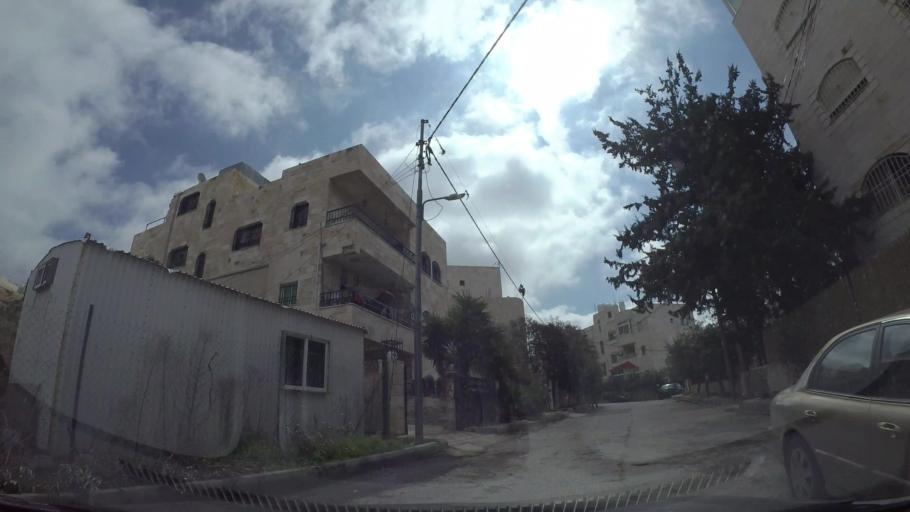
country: JO
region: Amman
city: Wadi as Sir
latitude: 31.9492
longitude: 35.8249
